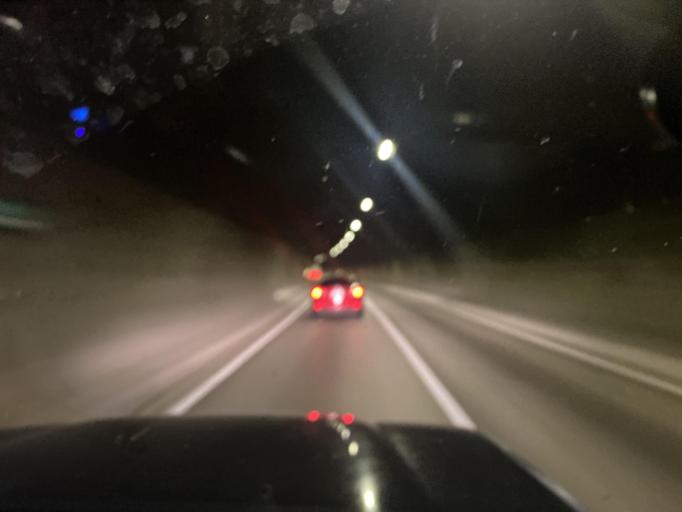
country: JP
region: Nagano
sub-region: Kitaazumi Gun
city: Hakuba
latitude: 36.8049
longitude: 137.9131
